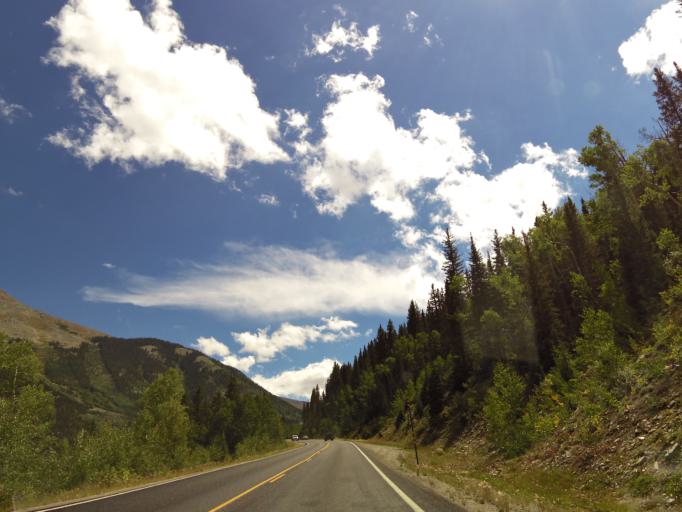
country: US
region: Colorado
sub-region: San Juan County
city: Silverton
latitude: 37.8015
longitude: -107.6770
